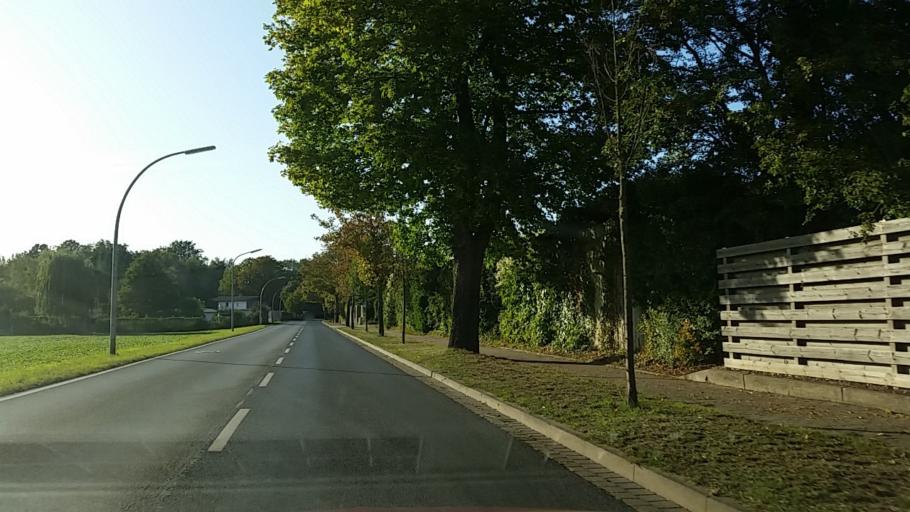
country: DE
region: Lower Saxony
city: Braunschweig
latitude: 52.2988
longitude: 10.5543
